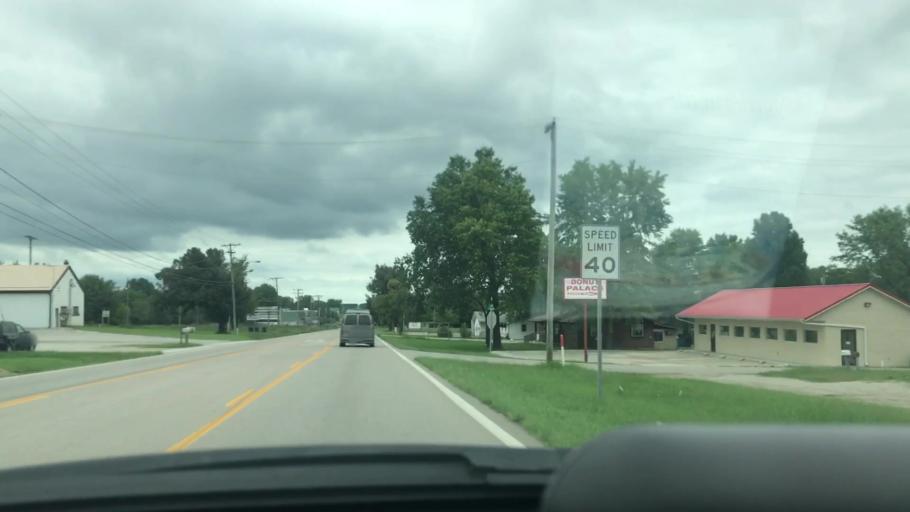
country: US
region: Missouri
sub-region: Dallas County
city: Buffalo
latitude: 37.6450
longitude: -93.1041
